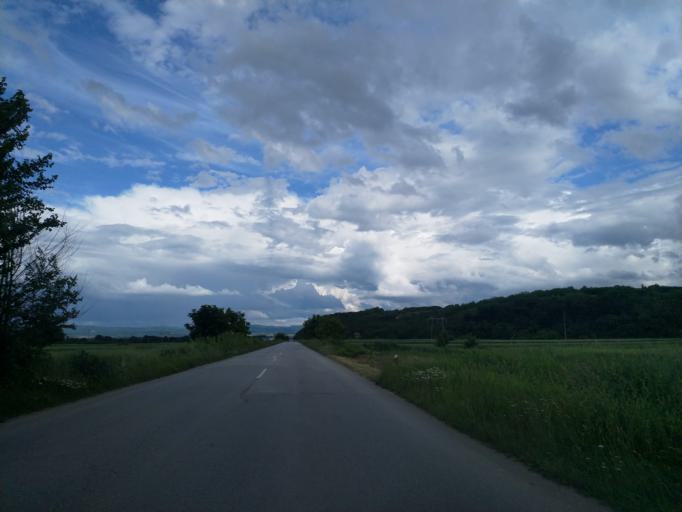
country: RS
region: Central Serbia
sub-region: Pomoravski Okrug
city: Jagodina
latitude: 43.9561
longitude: 21.3000
